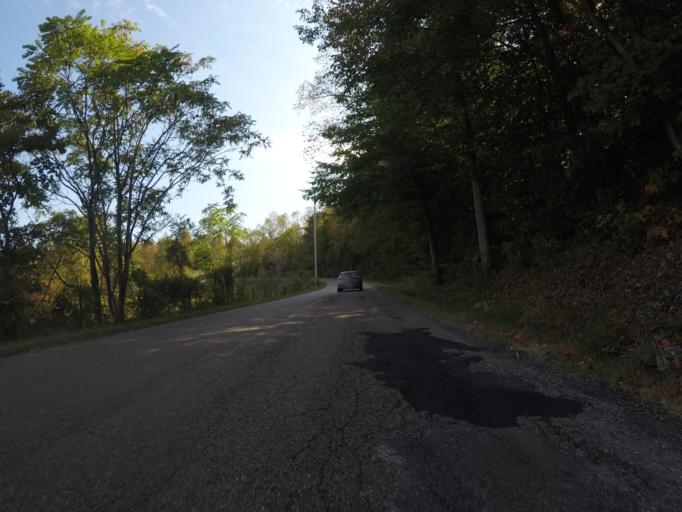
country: US
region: West Virginia
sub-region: Cabell County
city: Lesage
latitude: 38.5936
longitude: -82.4215
